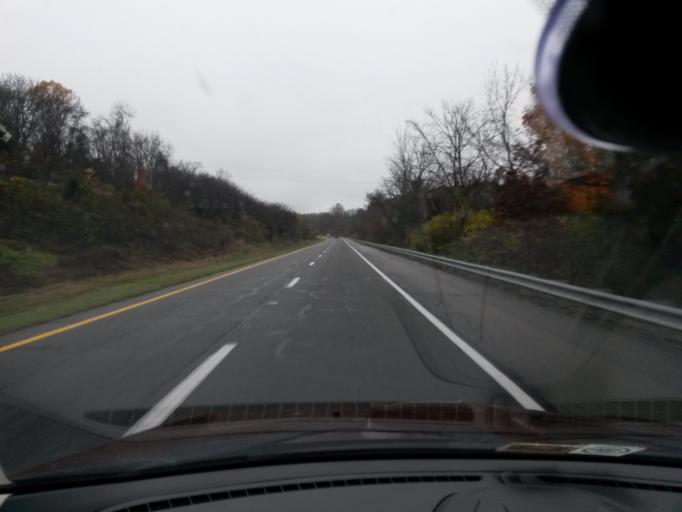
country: US
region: Virginia
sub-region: Botetourt County
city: Fincastle
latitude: 37.4644
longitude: -79.8819
